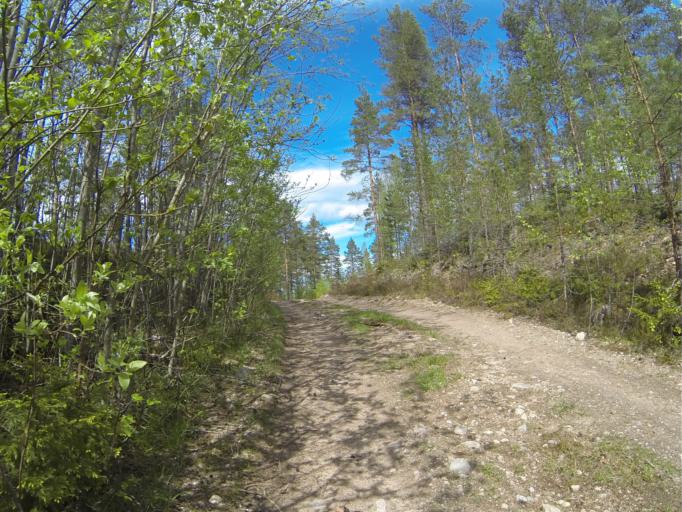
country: FI
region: Varsinais-Suomi
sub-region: Salo
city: Halikko
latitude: 60.3351
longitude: 23.0786
